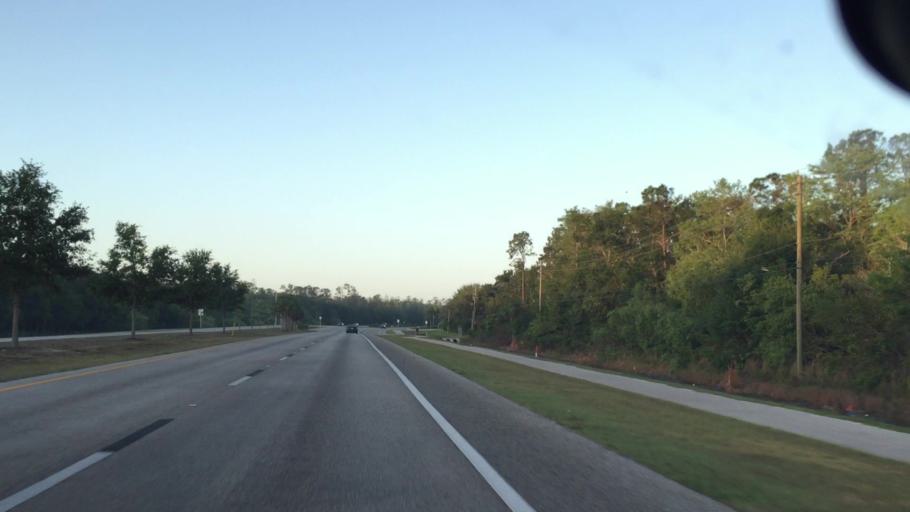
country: US
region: Florida
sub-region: Lee County
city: Villas
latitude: 26.5602
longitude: -81.8322
